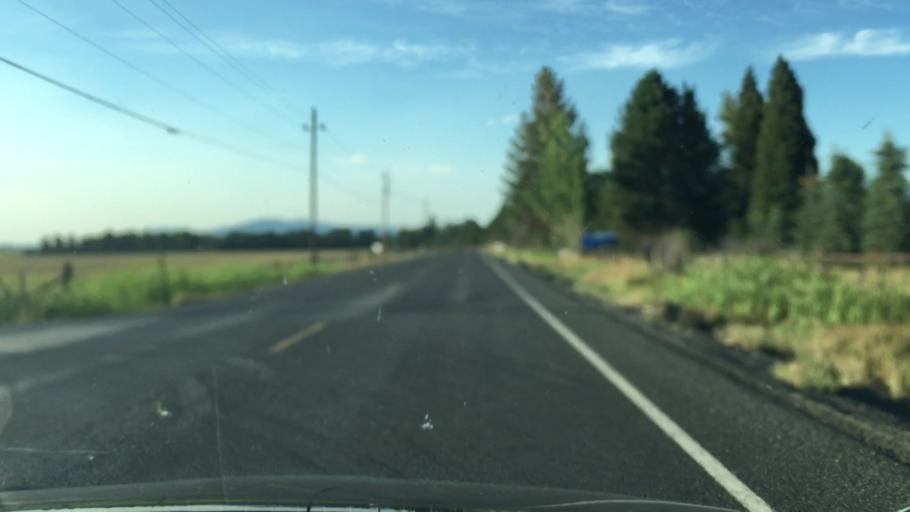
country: US
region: Idaho
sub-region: Valley County
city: McCall
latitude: 44.8181
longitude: -116.0780
